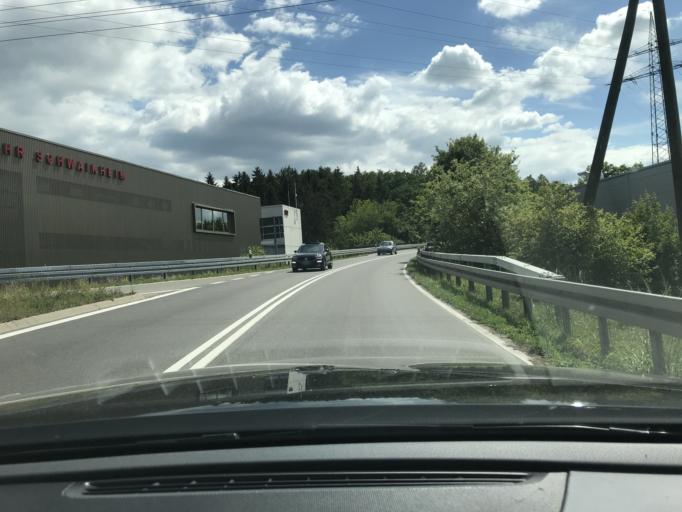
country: DE
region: Baden-Wuerttemberg
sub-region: Regierungsbezirk Stuttgart
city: Schwaikheim
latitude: 48.8686
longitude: 9.3618
